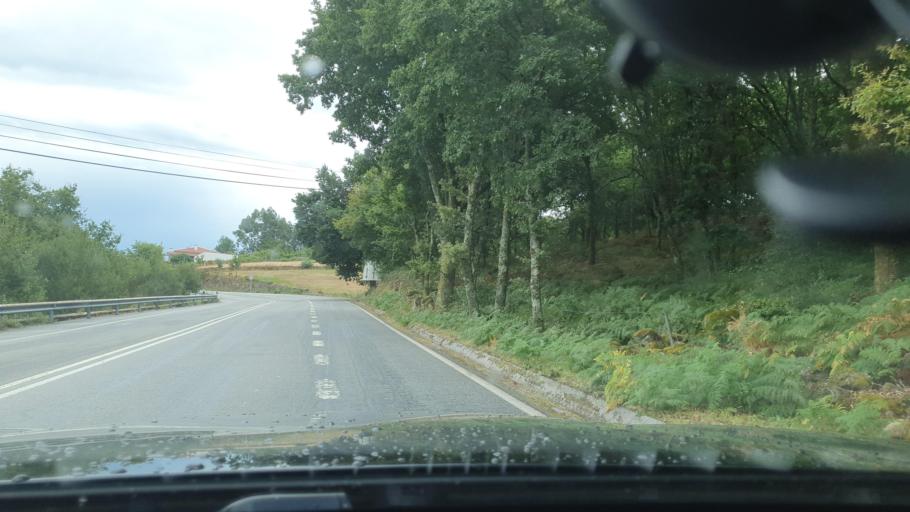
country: PT
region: Braga
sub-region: Vieira do Minho
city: Vieira do Minho
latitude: 41.6842
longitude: -8.0324
